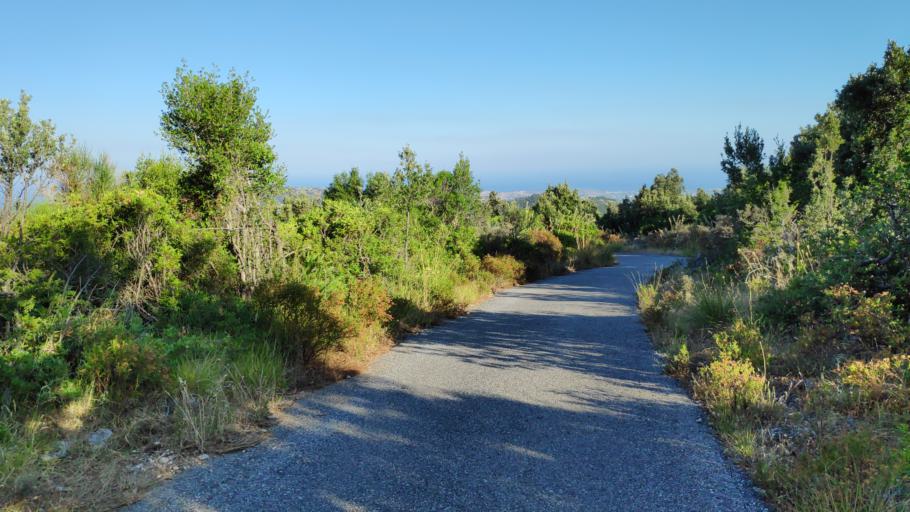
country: IT
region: Calabria
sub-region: Provincia di Reggio Calabria
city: Pazzano
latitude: 38.4524
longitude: 16.4348
